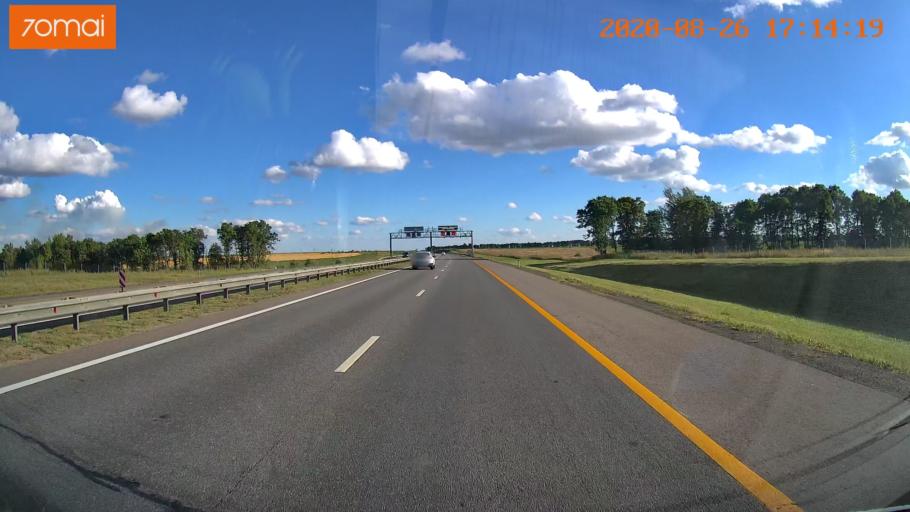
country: RU
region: Tula
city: Volovo
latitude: 53.6557
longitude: 38.0536
